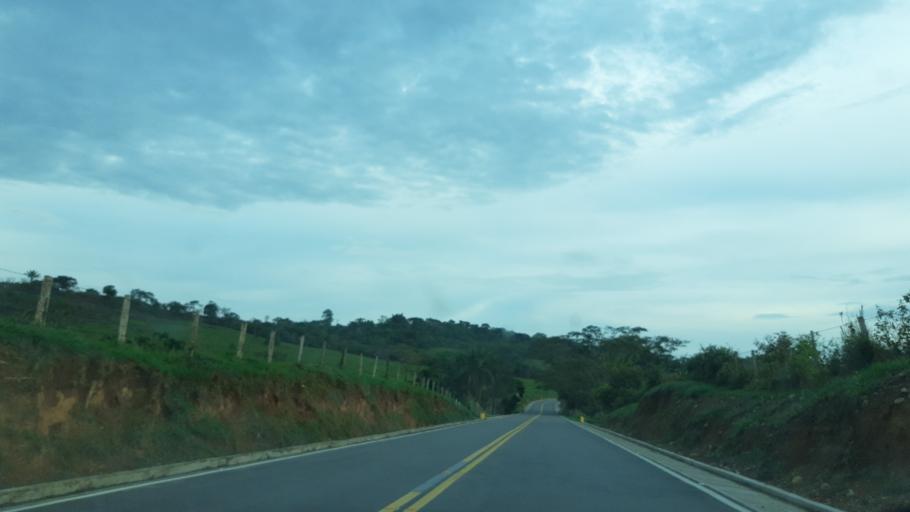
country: CO
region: Casanare
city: Sabanalarga
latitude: 4.8132
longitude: -73.0610
